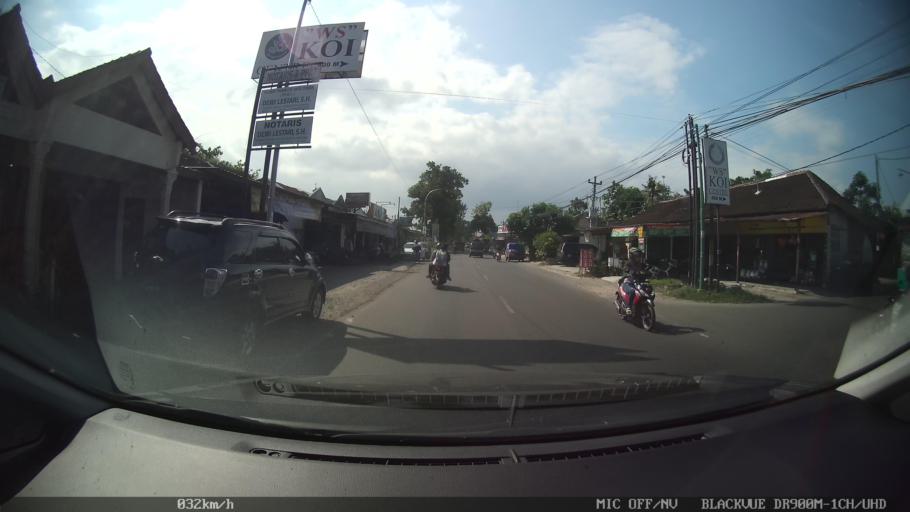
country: ID
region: Daerah Istimewa Yogyakarta
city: Sewon
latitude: -7.8683
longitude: 110.3905
